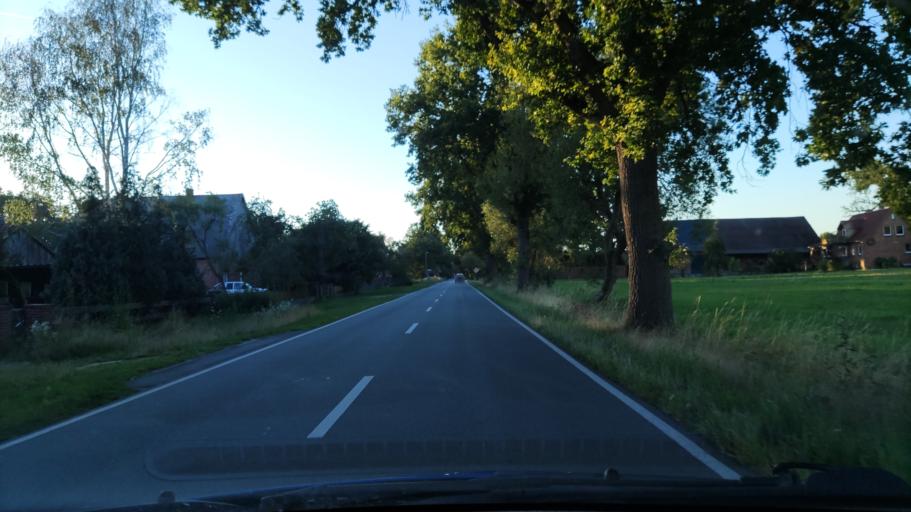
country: DE
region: Lower Saxony
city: Klein Gusborn
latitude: 53.0470
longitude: 11.1751
